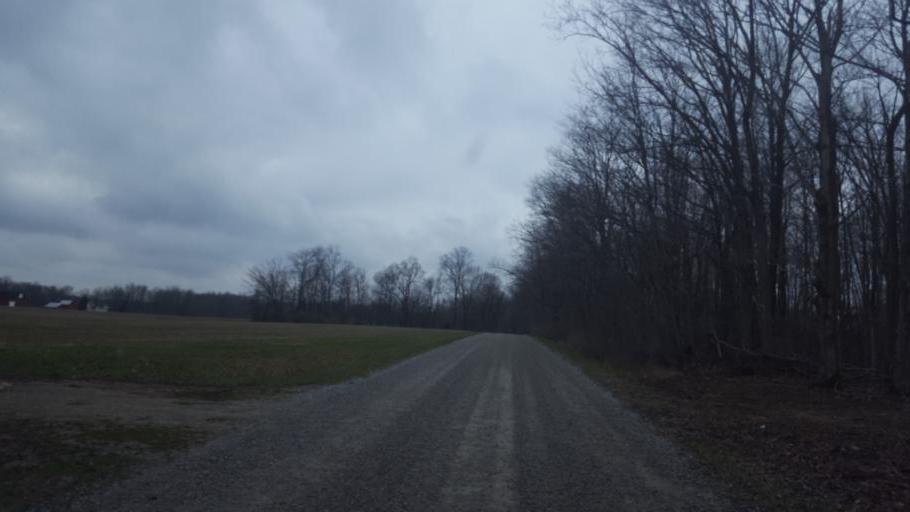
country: US
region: Ohio
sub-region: Delaware County
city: Ashley
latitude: 40.3737
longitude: -82.8782
